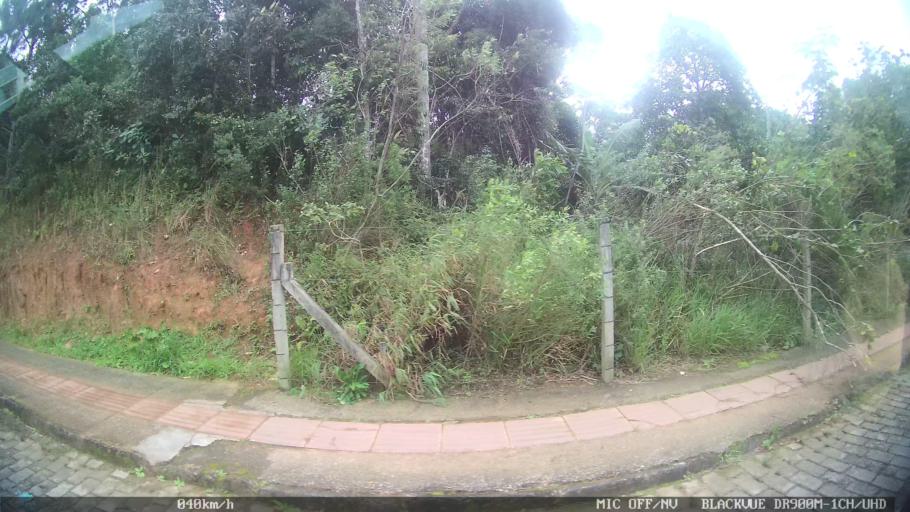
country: BR
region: Santa Catarina
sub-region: Sao Jose
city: Campinas
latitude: -27.5533
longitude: -48.6384
